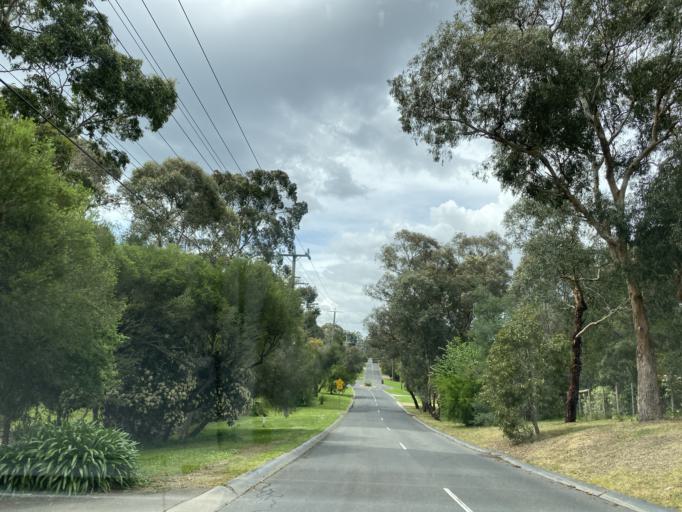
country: AU
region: Victoria
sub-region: Banyule
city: Lower Plenty
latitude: -37.7370
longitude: 145.1263
